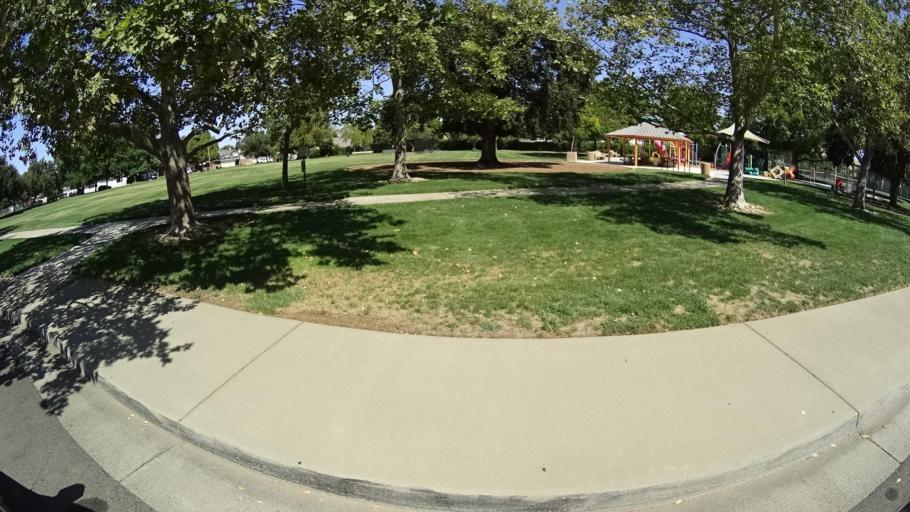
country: US
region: California
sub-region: Sacramento County
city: Laguna
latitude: 38.4159
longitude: -121.4101
